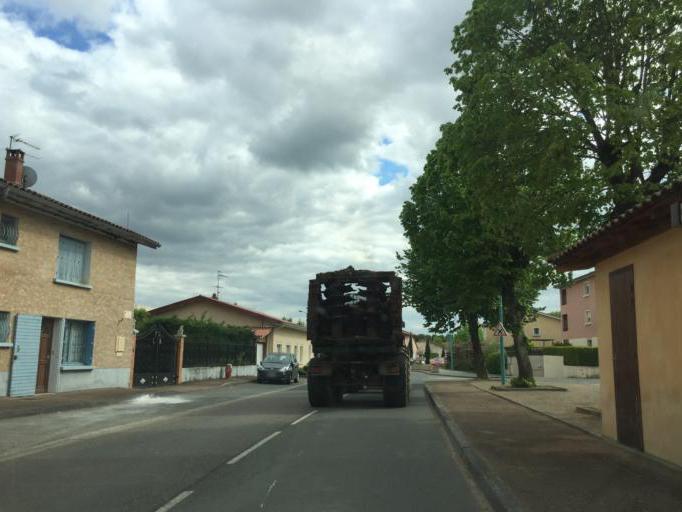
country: FR
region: Rhone-Alpes
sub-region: Departement de l'Ain
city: Amberieux-en-Dombes
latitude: 45.9964
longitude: 4.9045
